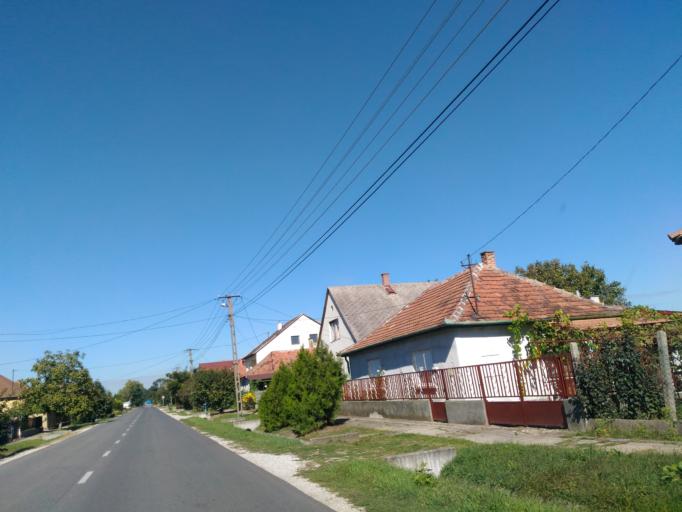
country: HU
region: Fejer
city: Pusztaszabolcs
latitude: 47.1488
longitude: 18.7480
